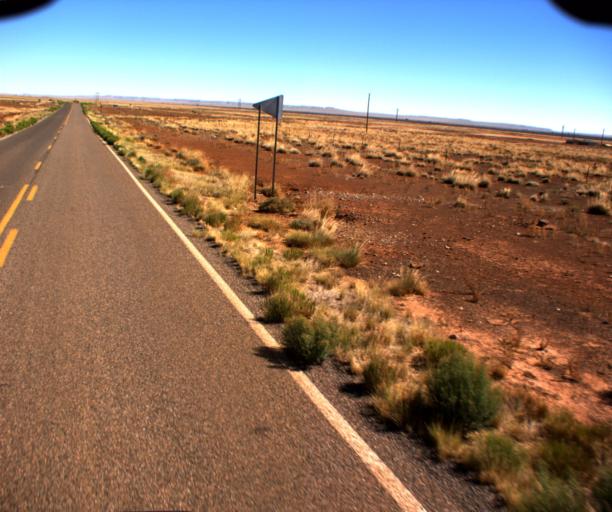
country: US
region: Arizona
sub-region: Coconino County
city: LeChee
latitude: 35.2448
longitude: -110.9607
